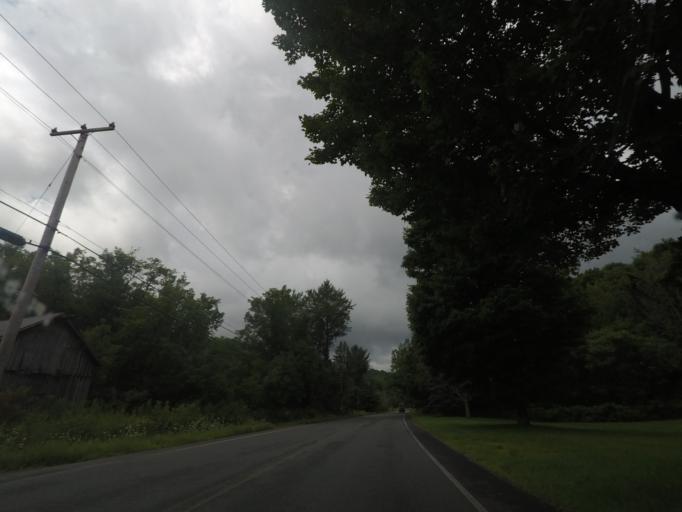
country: US
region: Massachusetts
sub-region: Berkshire County
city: Lanesborough
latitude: 42.5597
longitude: -73.2896
